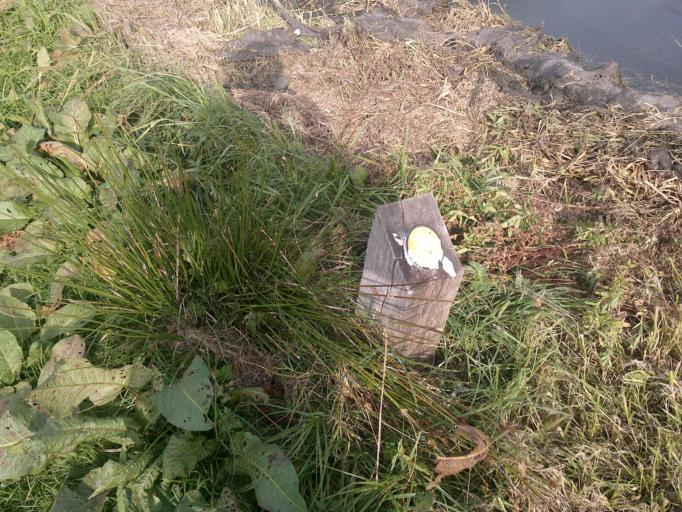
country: NL
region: South Holland
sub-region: Gemeente Voorschoten
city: Voorschoten
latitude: 52.1293
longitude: 4.4738
